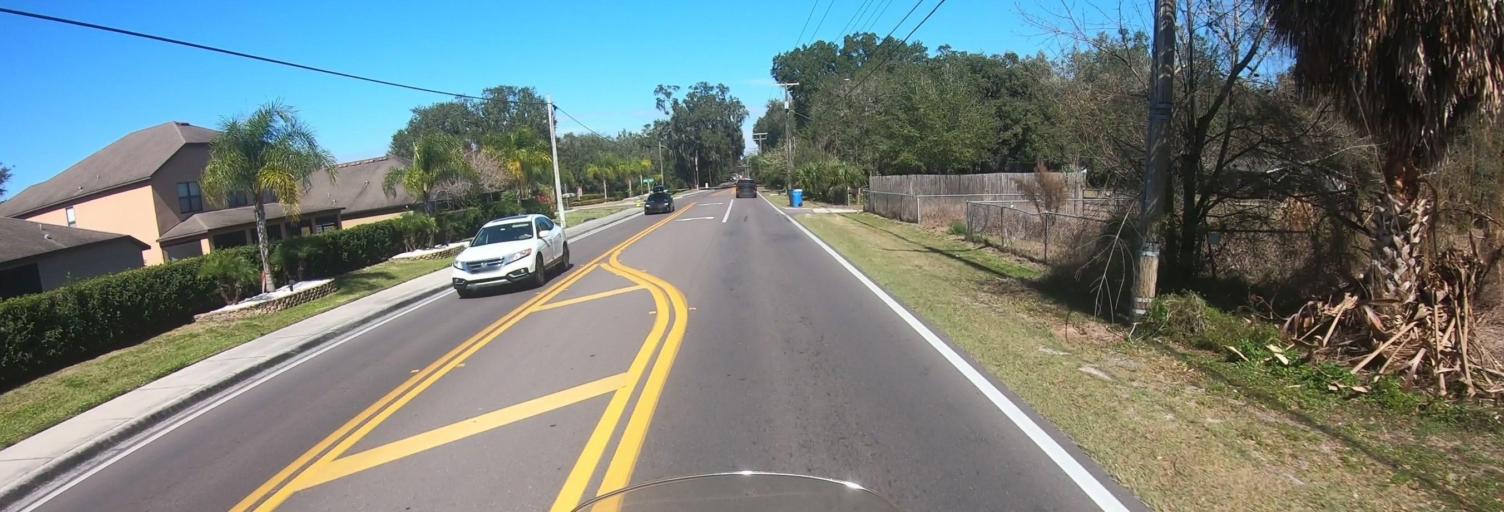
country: US
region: Florida
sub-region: Hillsborough County
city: Seffner
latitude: 27.9710
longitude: -82.2528
